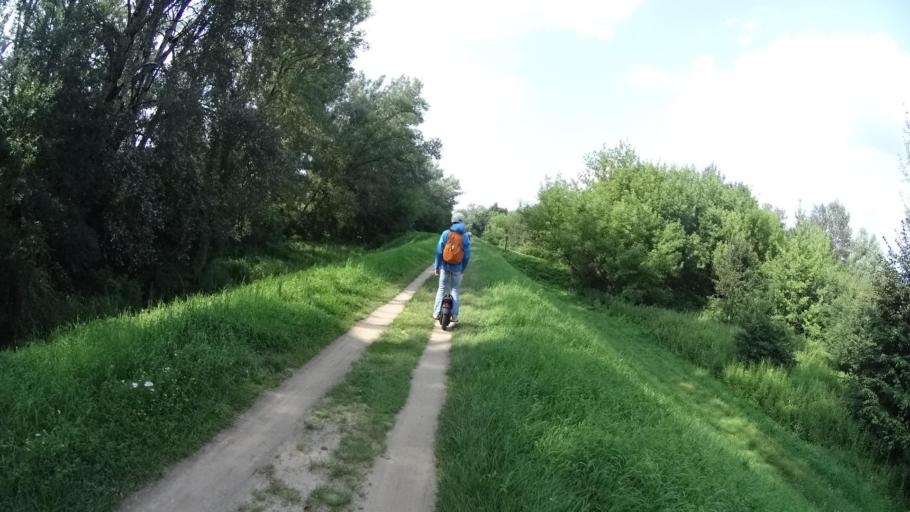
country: PL
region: Masovian Voivodeship
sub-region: Powiat legionowski
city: Jablonna
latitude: 52.3603
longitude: 20.9194
